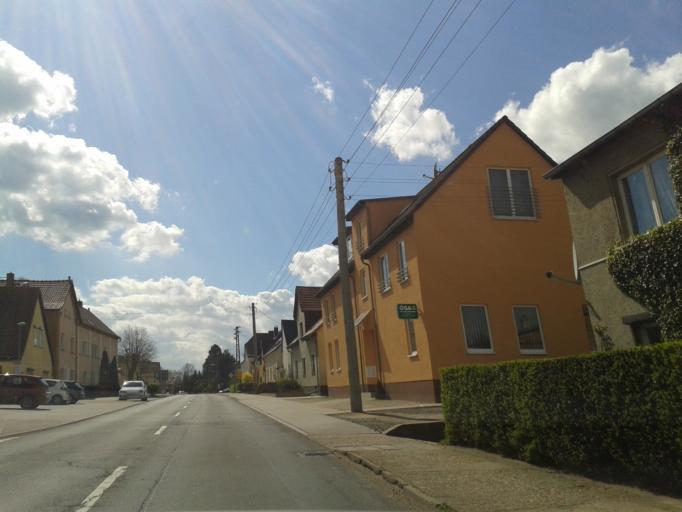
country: DE
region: Saxony-Anhalt
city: Teutschenthal
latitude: 51.4493
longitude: 11.8010
